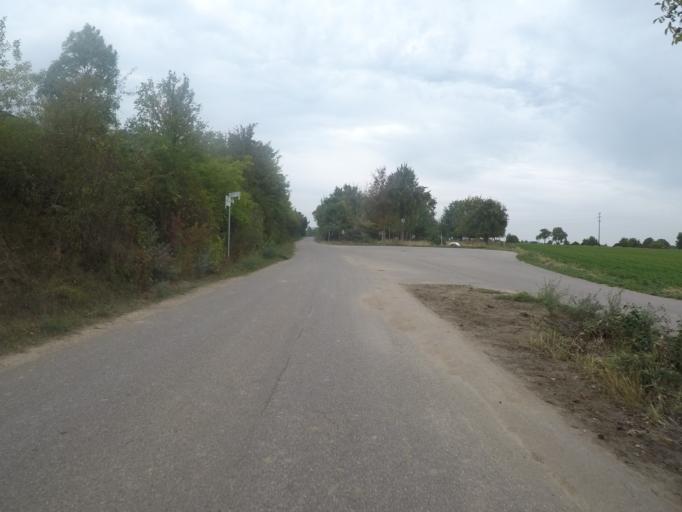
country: DE
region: Rheinland-Pfalz
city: Hassloch
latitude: 49.3750
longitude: 8.2615
